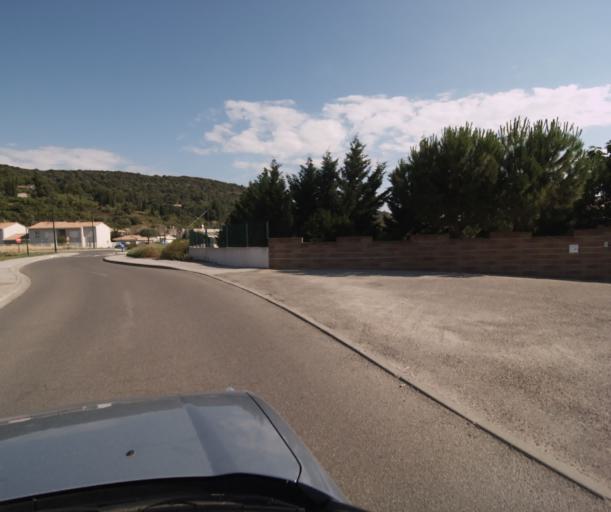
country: FR
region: Languedoc-Roussillon
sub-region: Departement de l'Aude
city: Limoux
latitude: 43.0734
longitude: 2.2175
